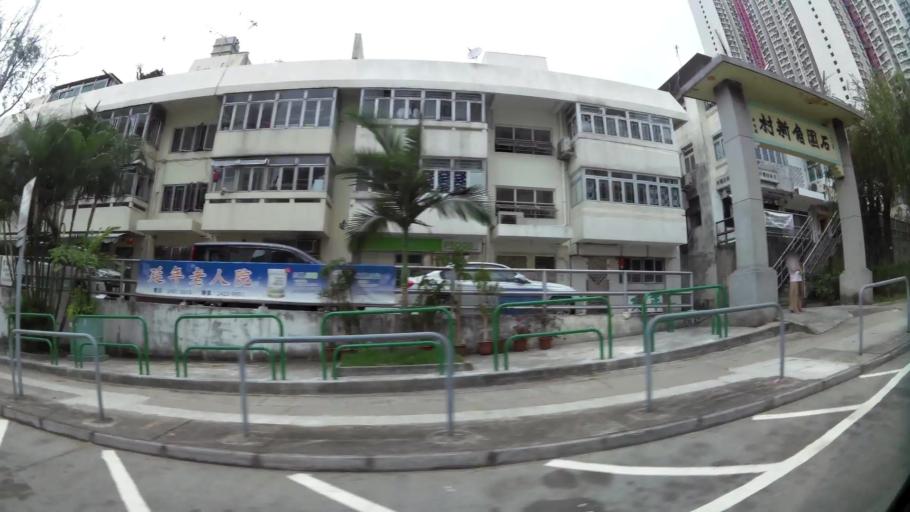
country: HK
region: Tsuen Wan
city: Tsuen Wan
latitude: 22.3757
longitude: 114.1365
